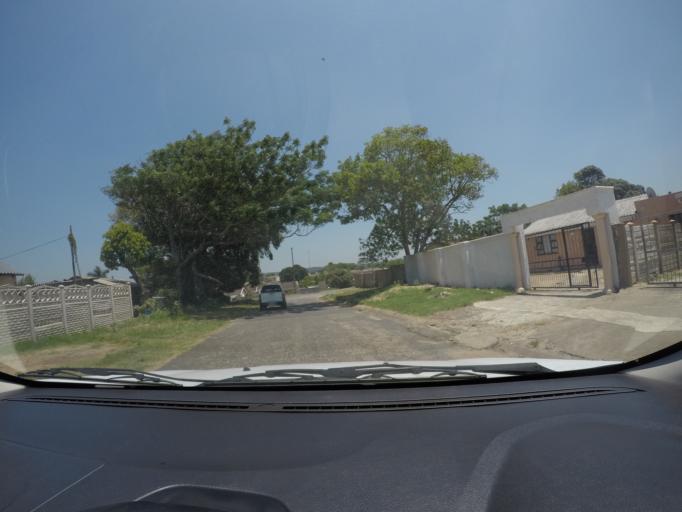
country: ZA
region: KwaZulu-Natal
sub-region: uThungulu District Municipality
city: eSikhawini
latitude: -28.8761
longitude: 31.9117
